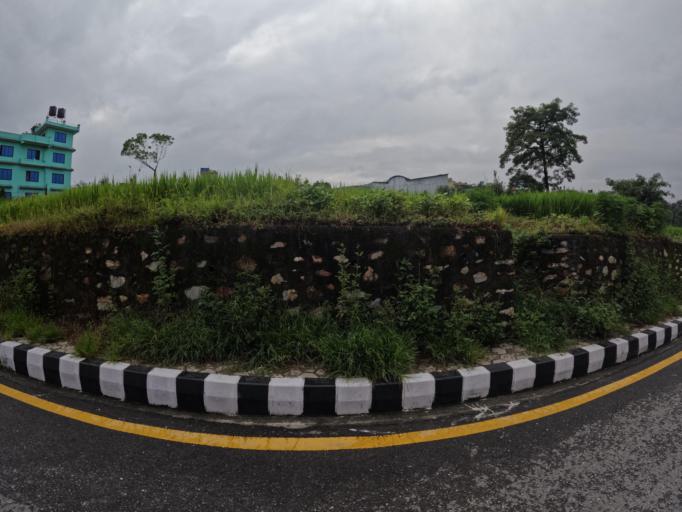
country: NP
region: Central Region
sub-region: Bagmati Zone
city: Kathmandu
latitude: 27.7605
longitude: 85.3274
